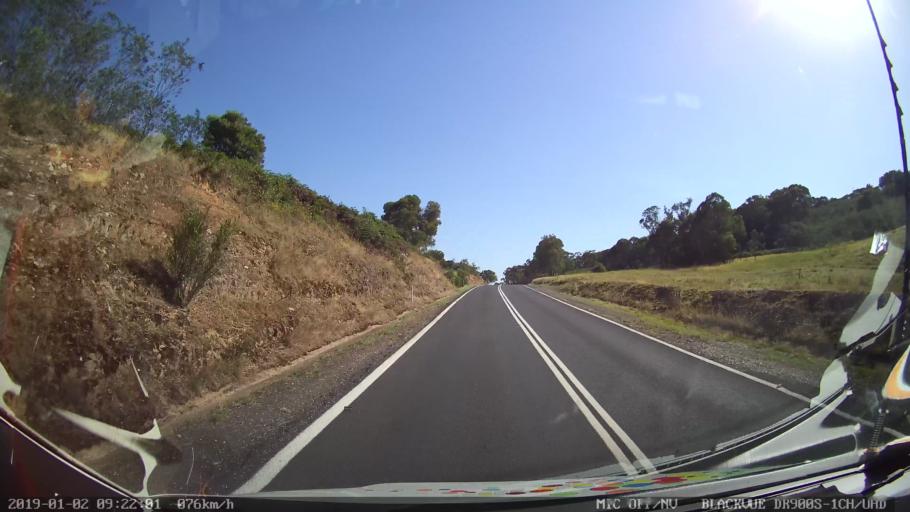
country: AU
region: New South Wales
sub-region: Tumut Shire
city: Tumut
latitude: -35.3992
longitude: 148.2893
